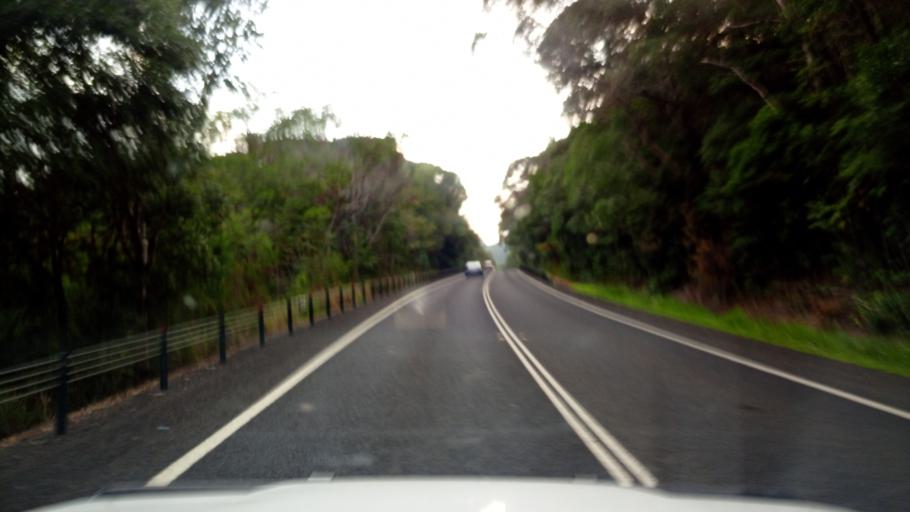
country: AU
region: Queensland
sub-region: Tablelands
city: Kuranda
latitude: -16.8373
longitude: 145.6181
